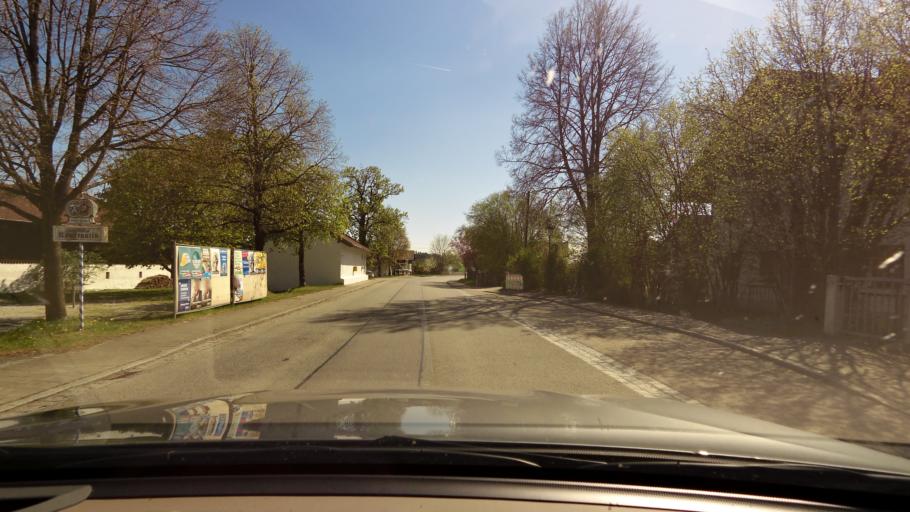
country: DE
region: Bavaria
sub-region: Upper Bavaria
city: Altdorf
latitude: 48.1536
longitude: 12.1835
